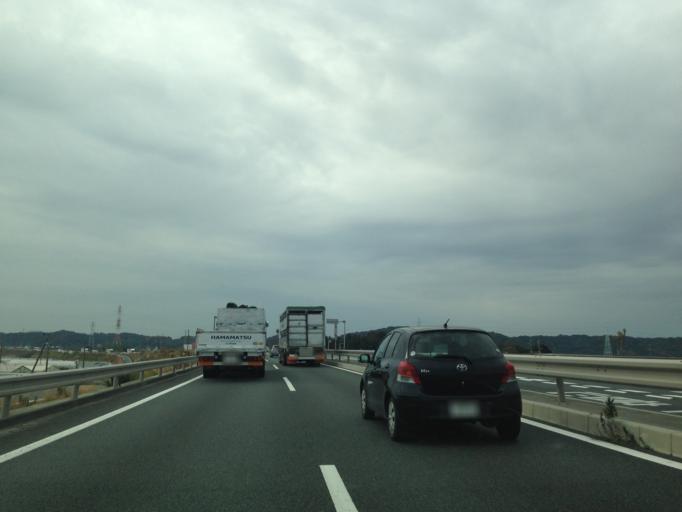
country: JP
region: Shizuoka
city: Fukuroi
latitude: 34.7484
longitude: 137.8961
